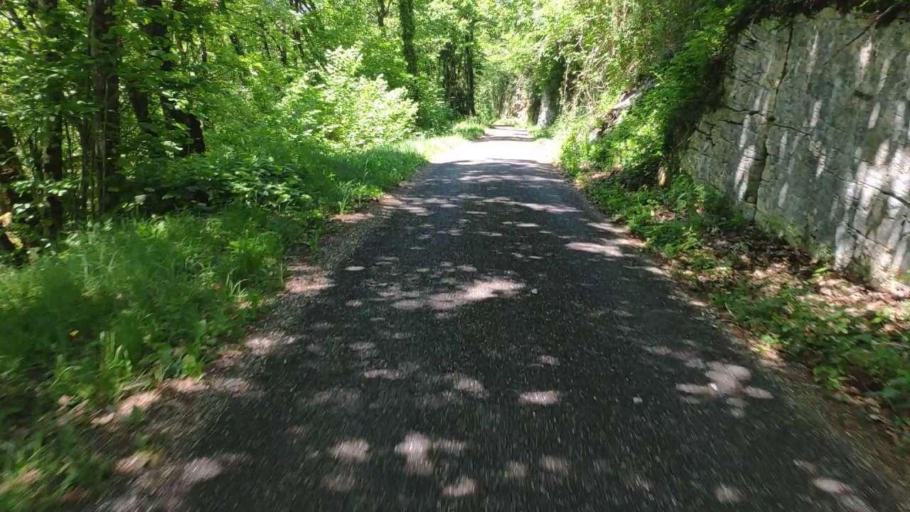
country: FR
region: Franche-Comte
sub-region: Departement du Jura
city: Poligny
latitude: 46.7492
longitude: 5.6805
